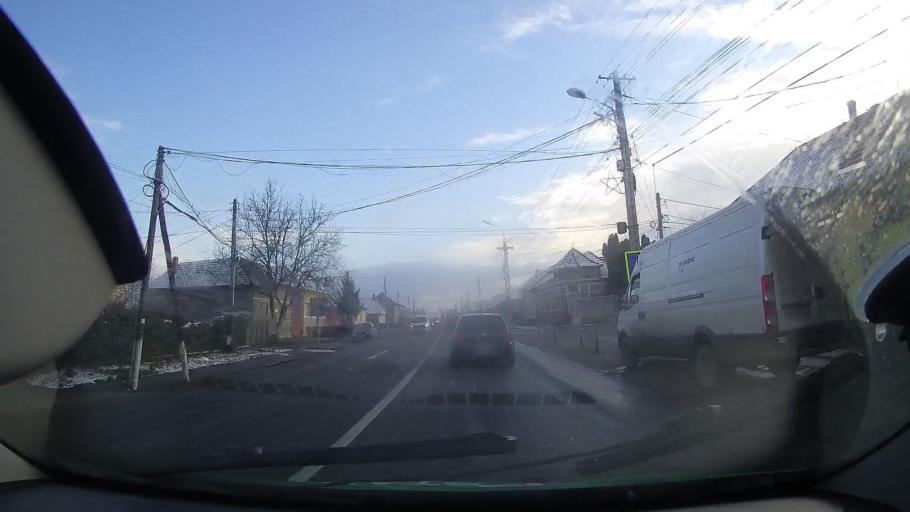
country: RO
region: Mures
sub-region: Comuna Iernut
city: Iernut
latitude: 46.4493
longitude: 24.2368
